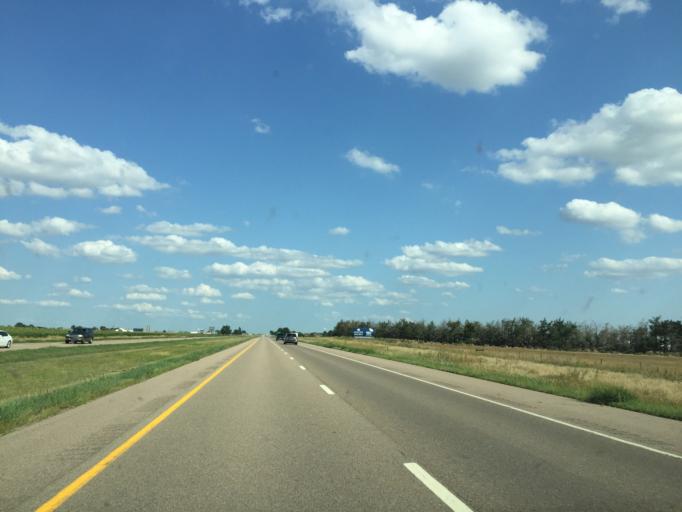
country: US
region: Kansas
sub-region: Gove County
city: Gove
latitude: 39.0634
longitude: -100.2536
